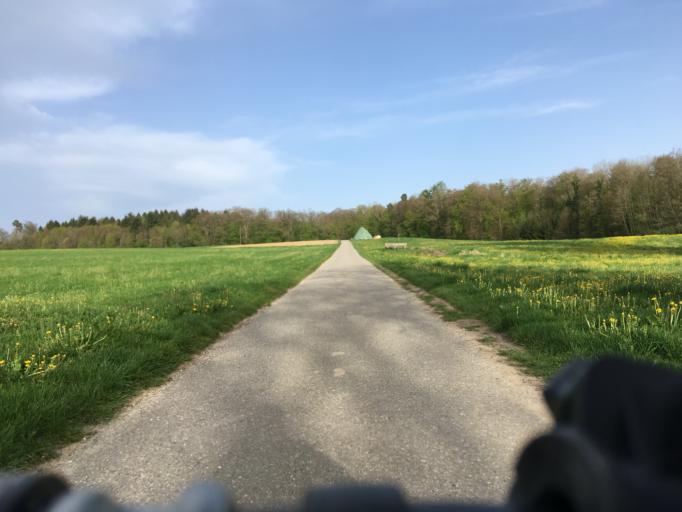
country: DE
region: Baden-Wuerttemberg
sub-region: Freiburg Region
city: Gailingen
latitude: 47.6853
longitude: 8.7786
